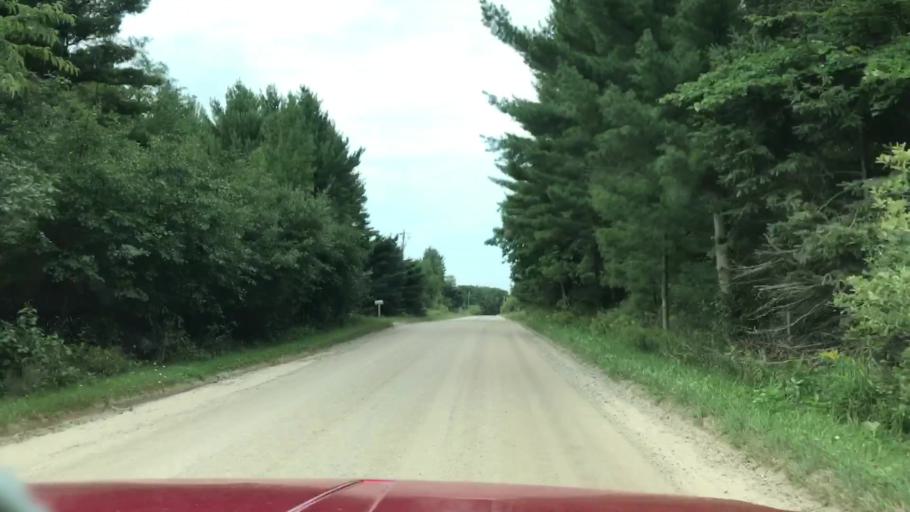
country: US
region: Michigan
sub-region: Charlevoix County
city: Charlevoix
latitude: 45.7271
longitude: -85.5485
